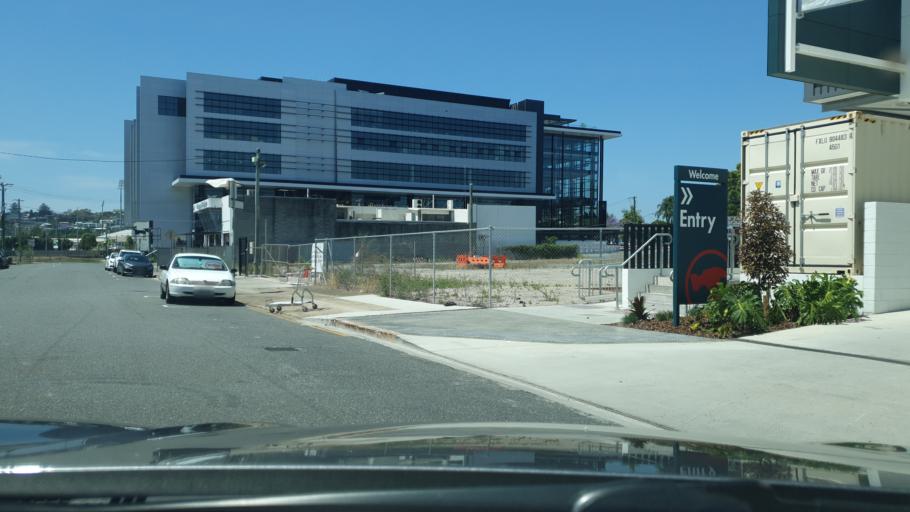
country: AU
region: Queensland
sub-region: Brisbane
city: Windsor
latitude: -27.4425
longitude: 153.0431
